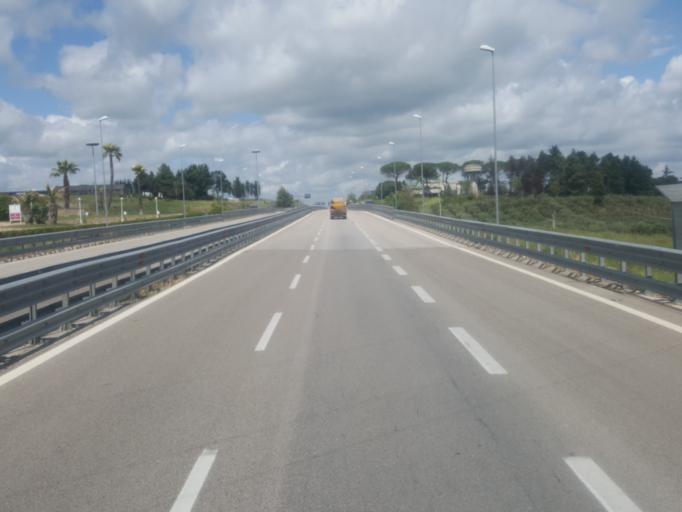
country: IT
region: Basilicate
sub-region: Provincia di Matera
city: Matera
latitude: 40.6990
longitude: 16.5888
